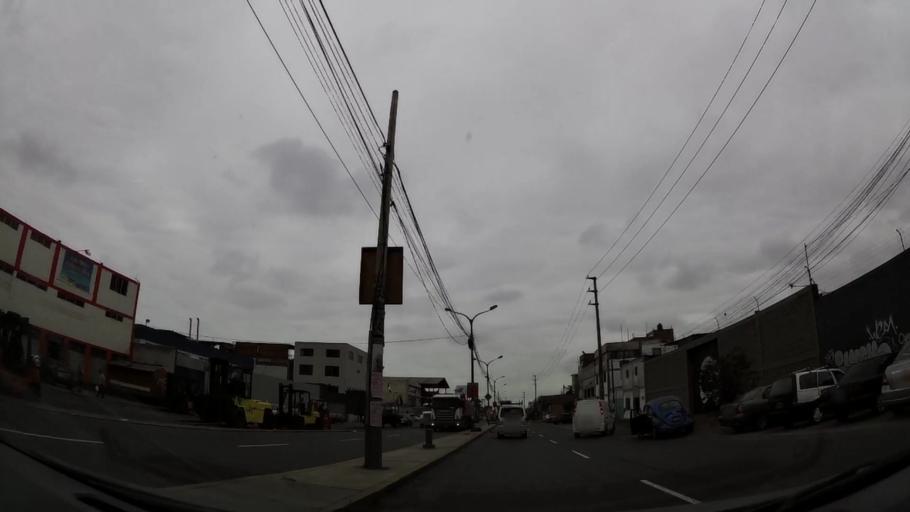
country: PE
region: Lima
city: Lima
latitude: -12.0455
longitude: -77.0659
